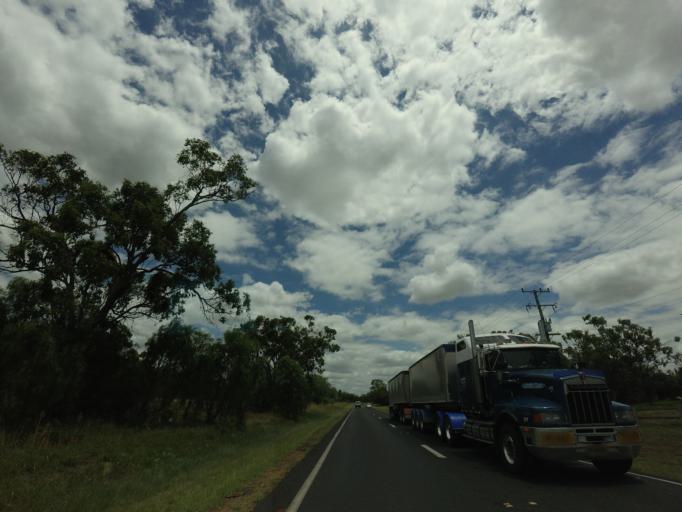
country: AU
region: New South Wales
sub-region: Moree Plains
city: Boggabilla
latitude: -28.5893
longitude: 150.3514
